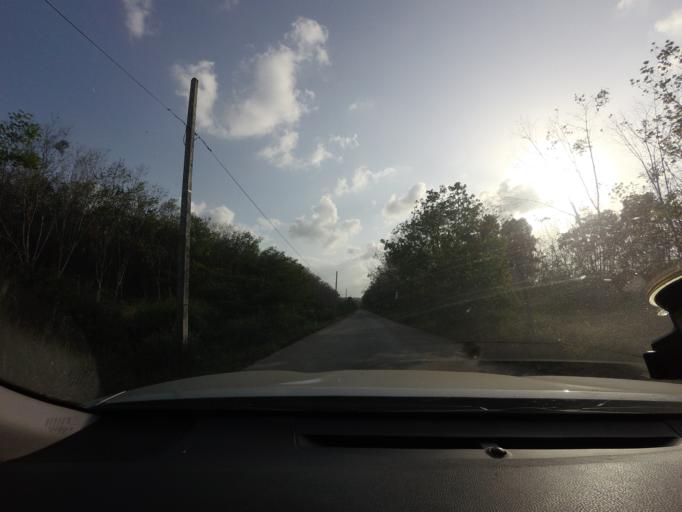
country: TH
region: Pattani
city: Mae Lan
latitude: 6.6210
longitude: 101.2489
